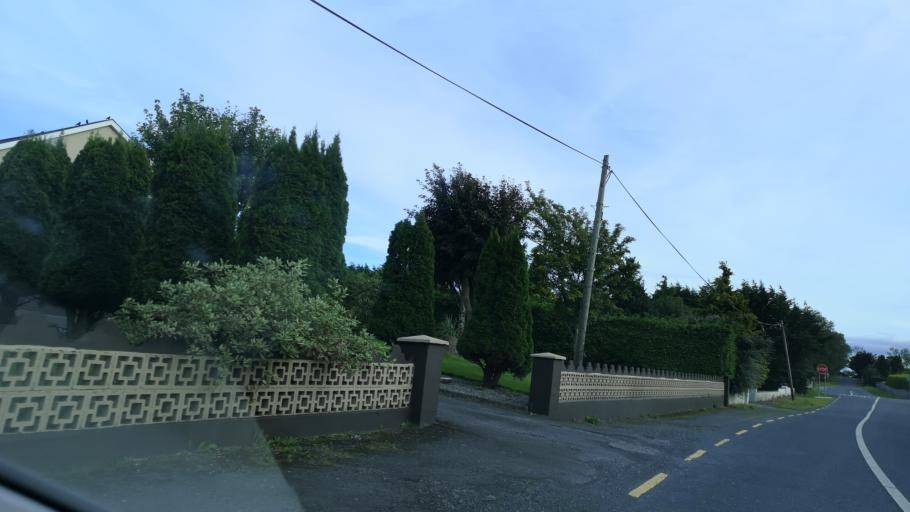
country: IE
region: Connaught
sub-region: County Galway
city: Ballinasloe
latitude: 53.3127
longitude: -8.2802
